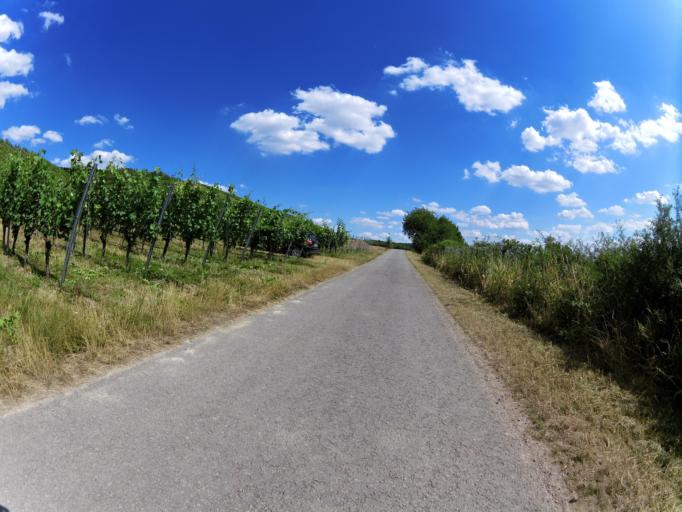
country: DE
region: Bavaria
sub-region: Regierungsbezirk Unterfranken
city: Thungersheim
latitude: 49.8918
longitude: 9.8372
